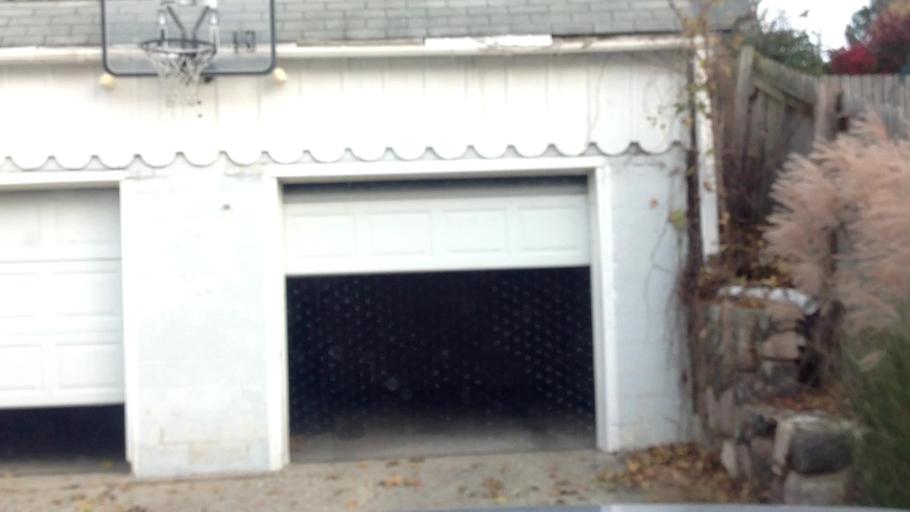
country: US
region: Michigan
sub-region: Oakland County
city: Sylvan Lake
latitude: 42.6307
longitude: -83.3389
